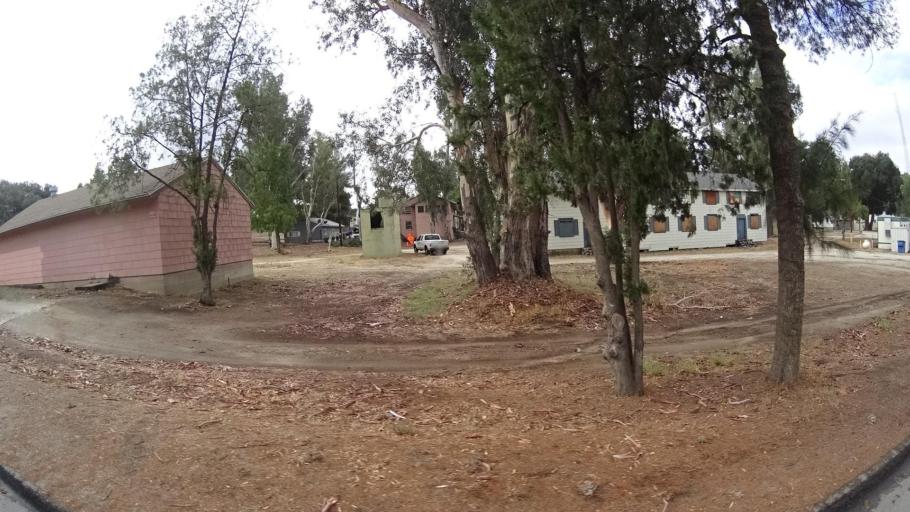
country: US
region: California
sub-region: San Diego County
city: Campo
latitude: 32.6076
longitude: -116.4704
